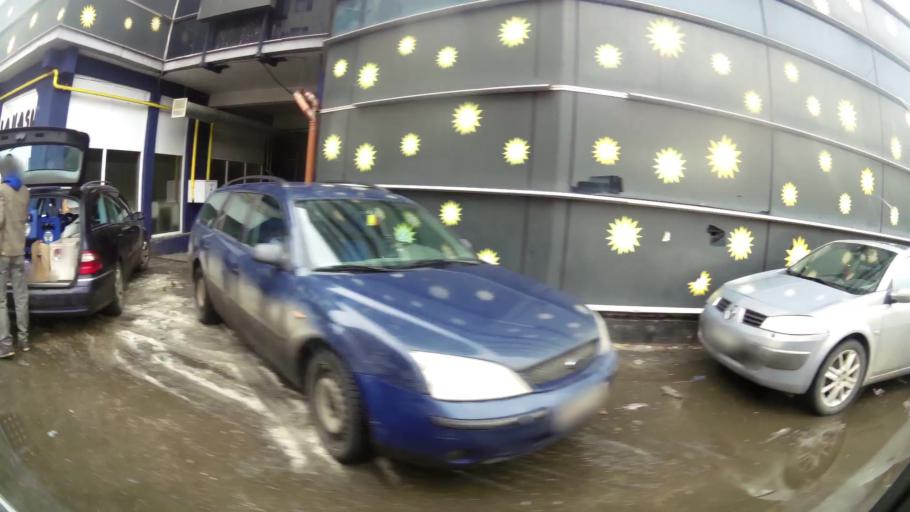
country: RO
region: Bucuresti
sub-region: Municipiul Bucuresti
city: Bucuresti
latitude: 44.4199
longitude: 26.0661
